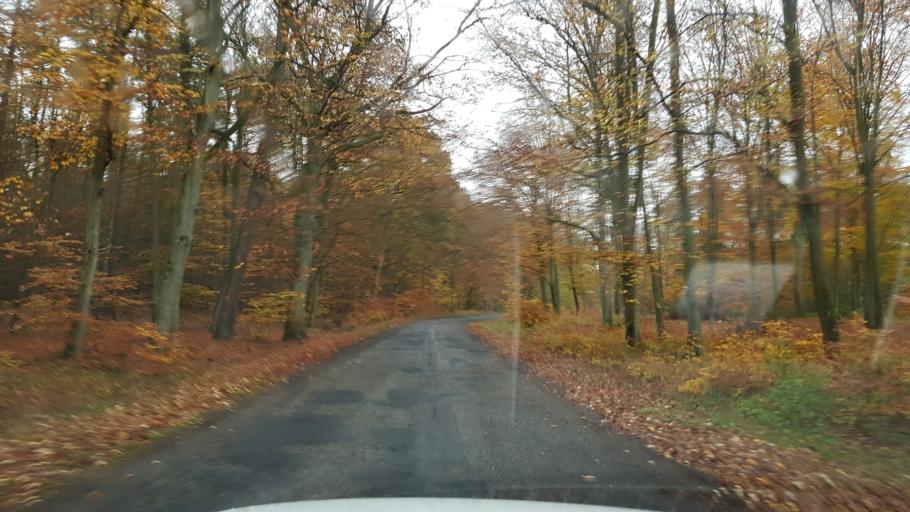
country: PL
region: West Pomeranian Voivodeship
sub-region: Powiat goleniowski
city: Stepnica
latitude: 53.6581
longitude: 14.6883
